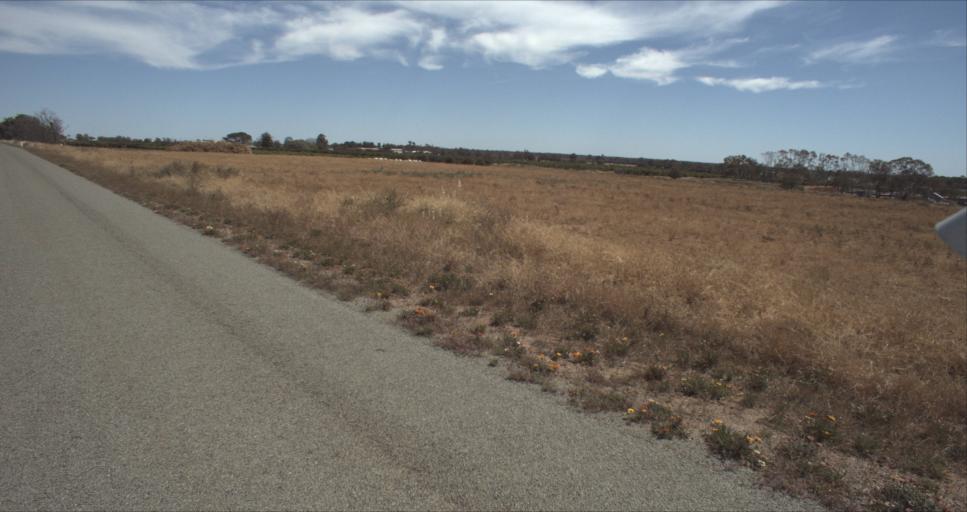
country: AU
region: New South Wales
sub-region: Leeton
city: Leeton
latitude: -34.6091
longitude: 146.4349
